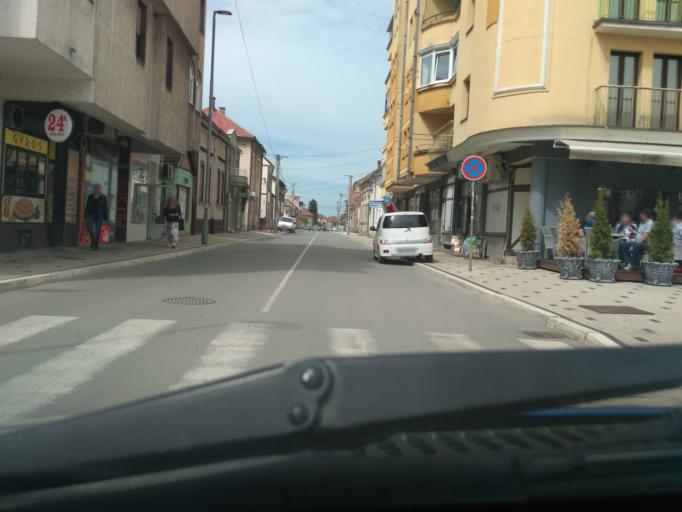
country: RS
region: Central Serbia
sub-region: Pomoravski Okrug
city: Svilajnac
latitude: 44.2347
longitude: 21.1964
